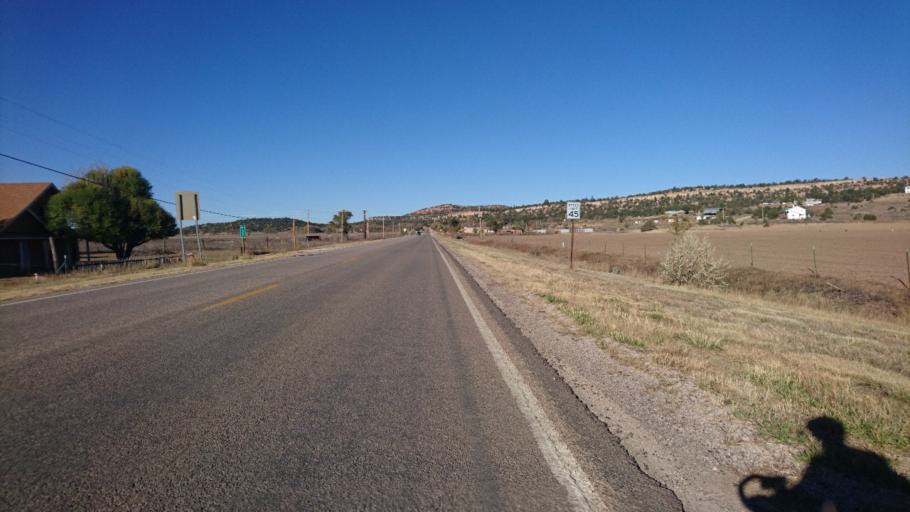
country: US
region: New Mexico
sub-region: McKinley County
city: Black Rock
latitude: 35.1333
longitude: -108.5026
